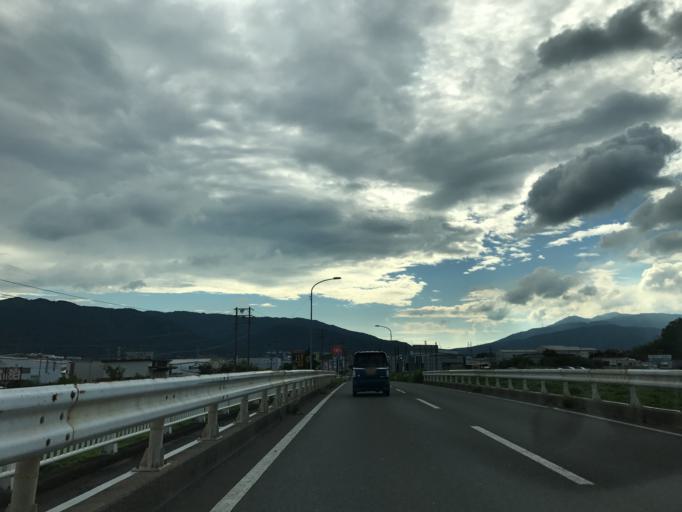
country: JP
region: Gifu
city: Tarui
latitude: 35.3665
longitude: 136.5493
